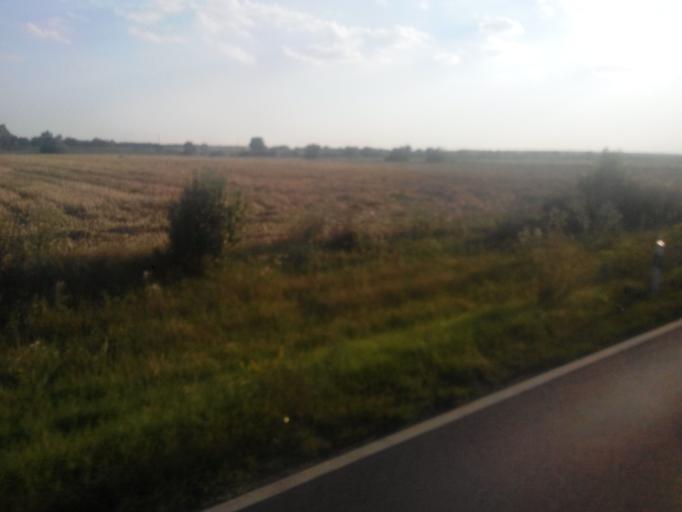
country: HU
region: Csongrad
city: Apatfalva
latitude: 46.1647
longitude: 20.6348
